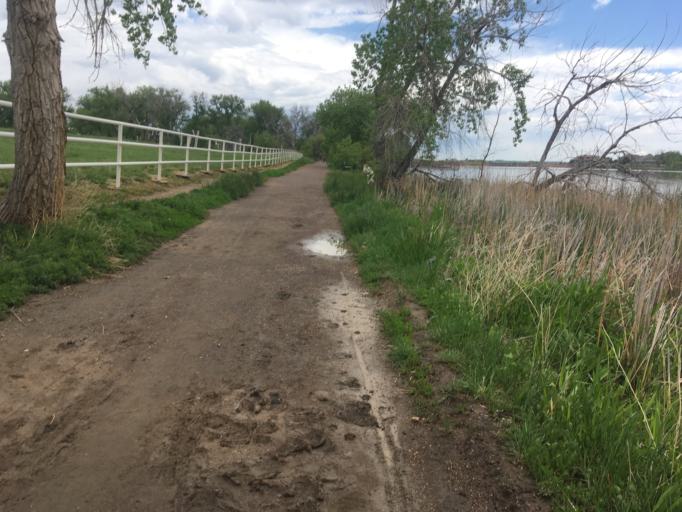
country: US
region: Colorado
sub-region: Adams County
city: Northglenn
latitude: 39.9555
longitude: -105.0137
